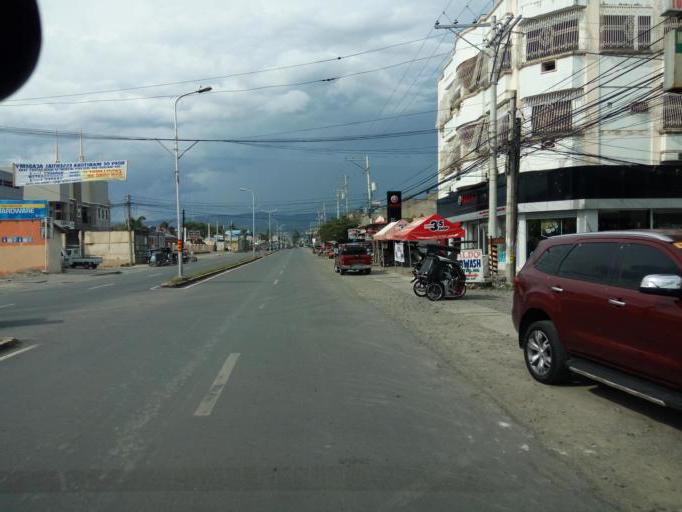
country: PH
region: Central Luzon
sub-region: Province of Nueva Ecija
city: Sibul
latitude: 15.7984
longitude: 120.9951
